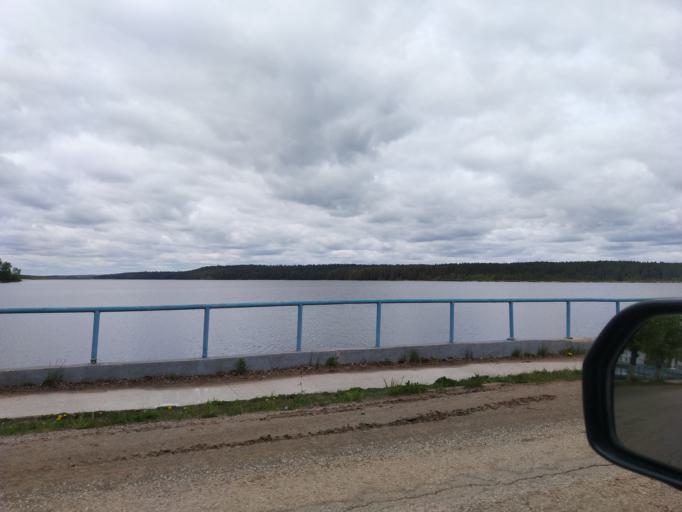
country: RU
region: Perm
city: Pavlovskiy
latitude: 57.8436
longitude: 54.8395
